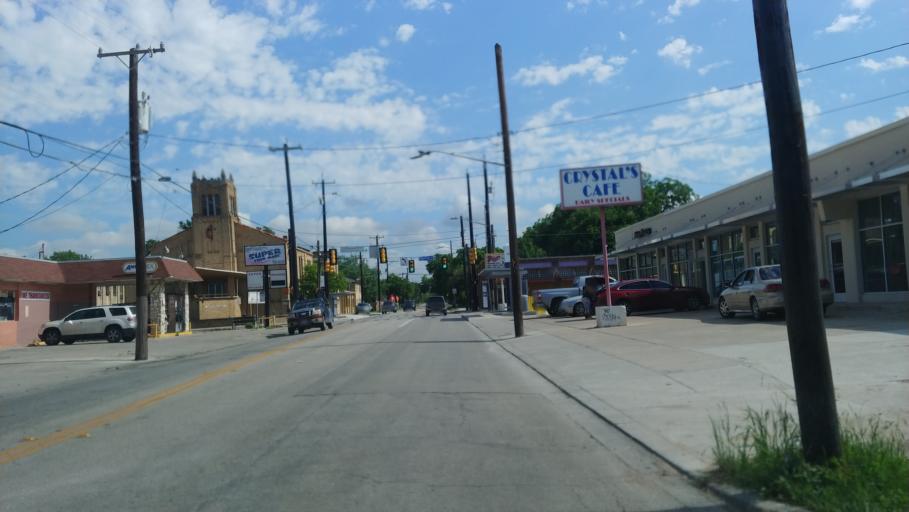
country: US
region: Texas
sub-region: Bexar County
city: San Antonio
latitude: 29.4532
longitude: -98.5239
